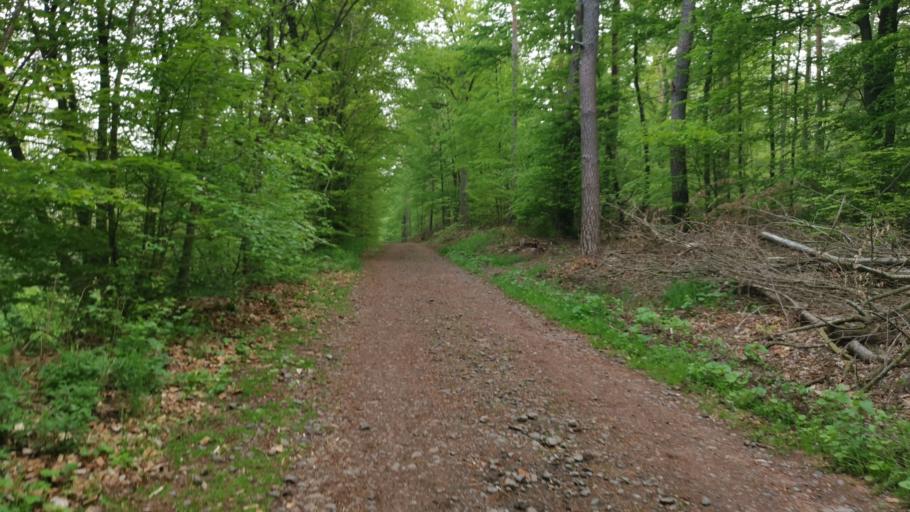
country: DE
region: Saarland
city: Sankt Ingbert
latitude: 49.2640
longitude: 7.1719
